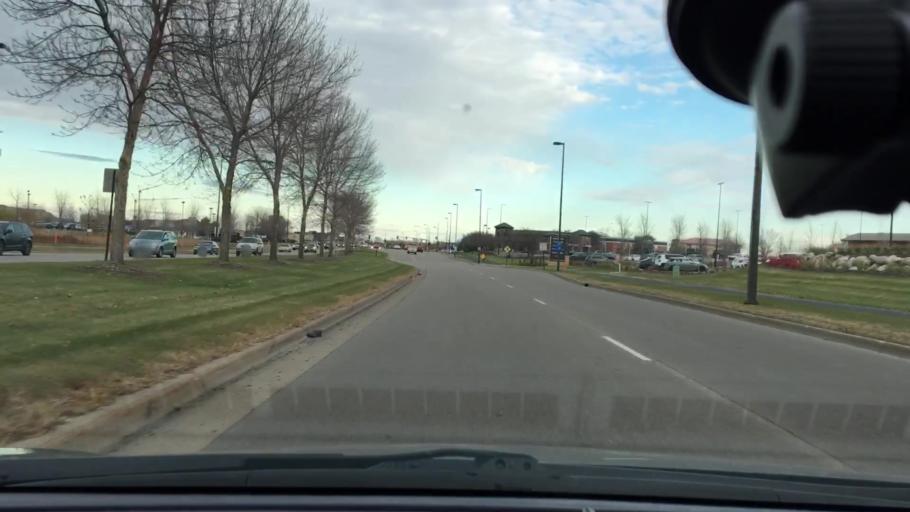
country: US
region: Minnesota
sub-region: Hennepin County
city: Maple Grove
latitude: 45.0941
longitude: -93.4363
